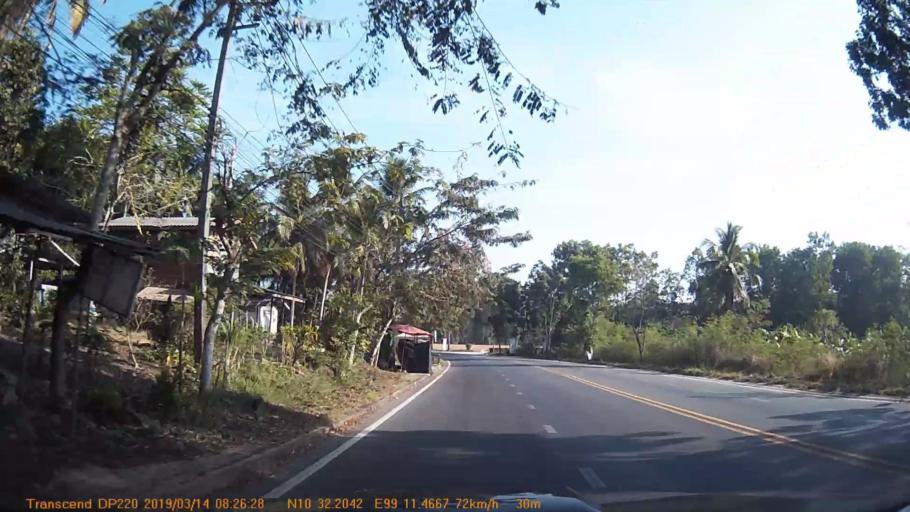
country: TH
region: Chumphon
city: Chumphon
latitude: 10.5367
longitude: 99.1909
